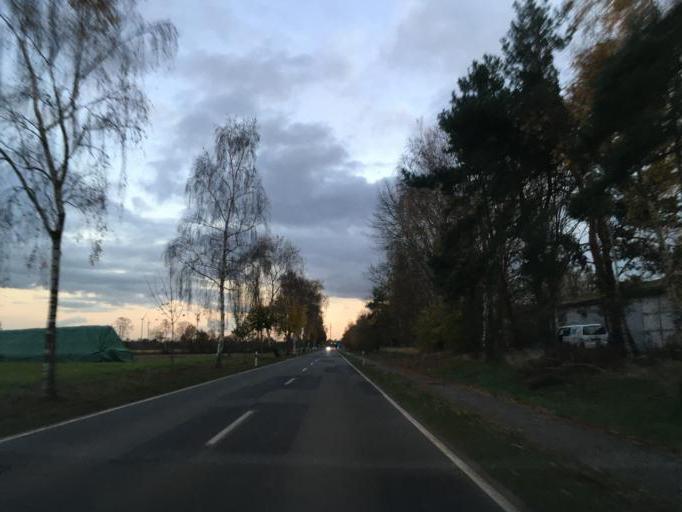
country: DE
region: Lower Saxony
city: Stelle
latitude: 53.3574
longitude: 10.1409
